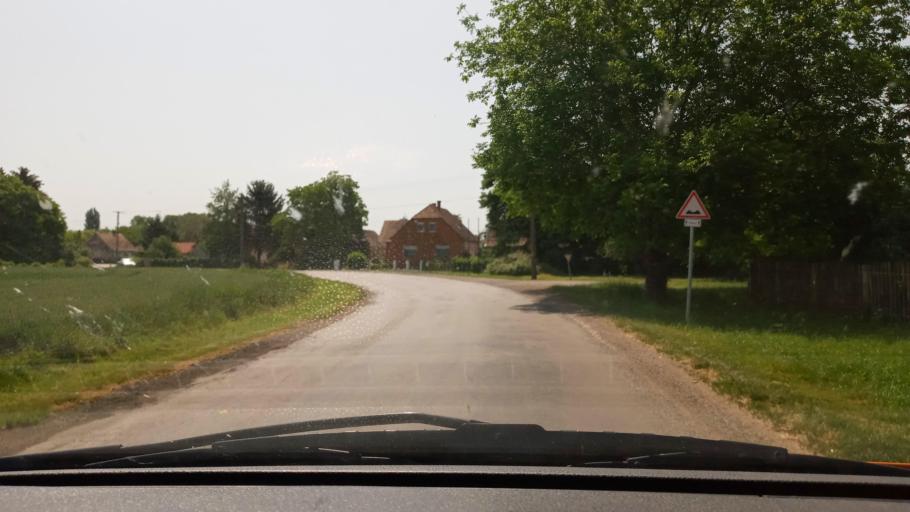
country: HU
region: Baranya
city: Szentlorinc
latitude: 46.0122
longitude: 18.0390
